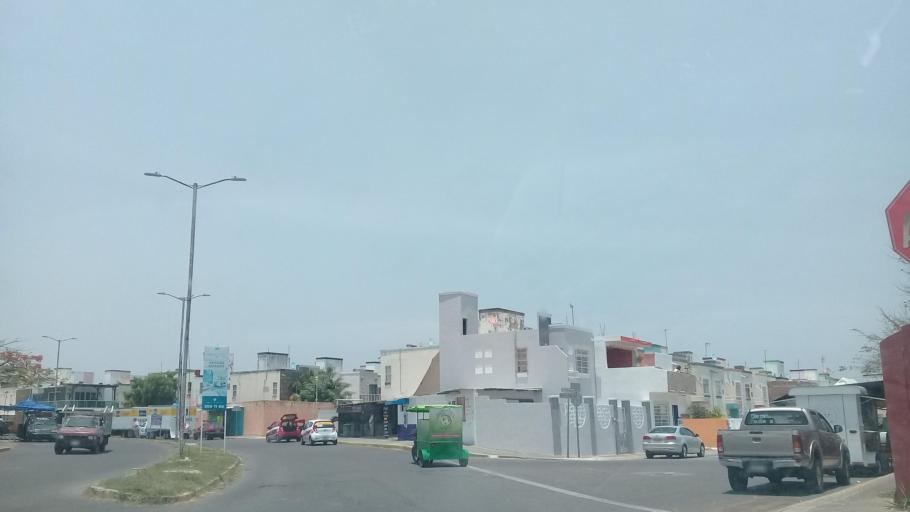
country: MX
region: Veracruz
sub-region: Veracruz
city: Hacienda Sotavento
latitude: 19.1299
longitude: -96.1745
